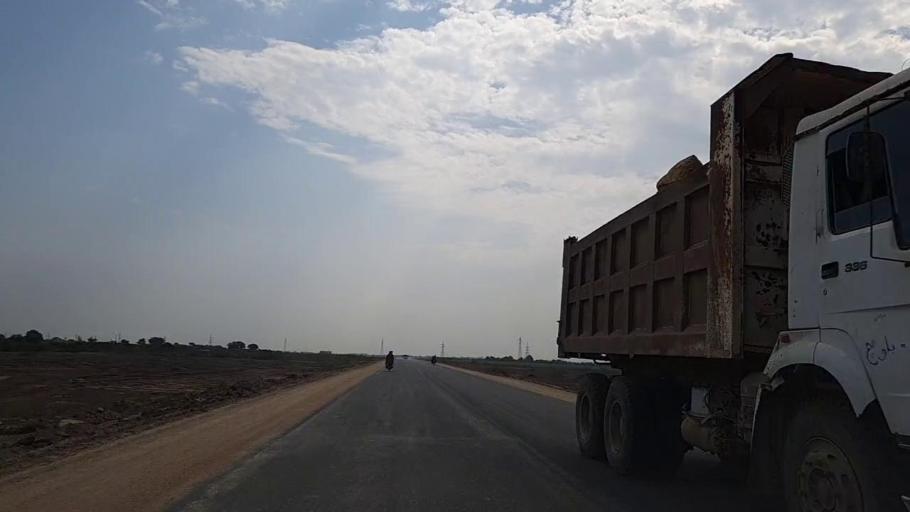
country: PK
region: Sindh
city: Naukot
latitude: 24.9613
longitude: 69.2828
